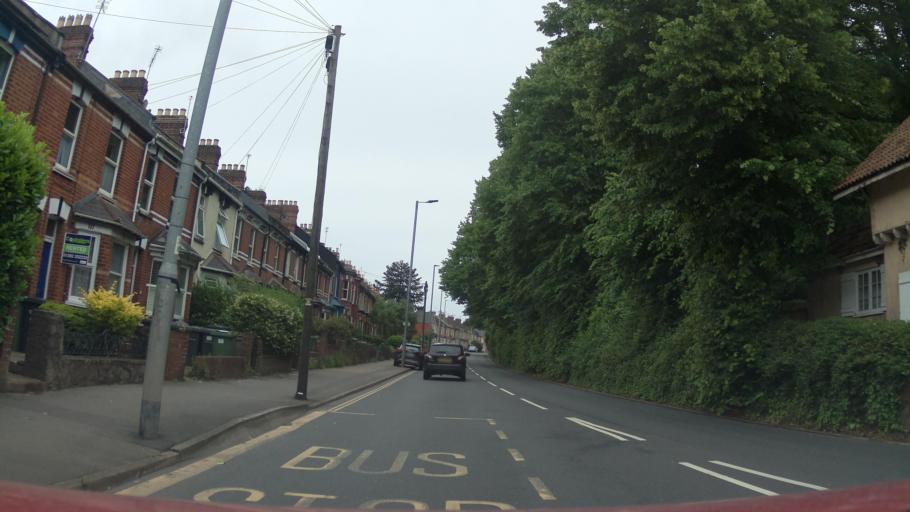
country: GB
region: England
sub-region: Devon
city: Heavitree
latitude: 50.7213
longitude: -3.5004
